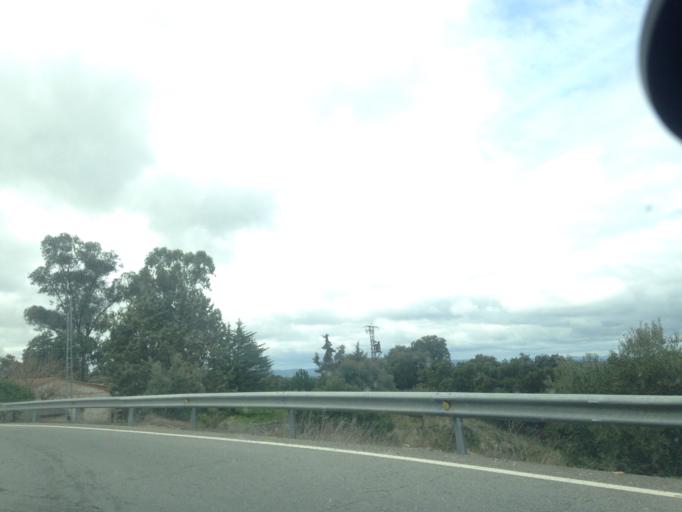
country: ES
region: Extremadura
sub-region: Provincia de Caceres
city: Montanchez
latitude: 39.2313
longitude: -6.1626
